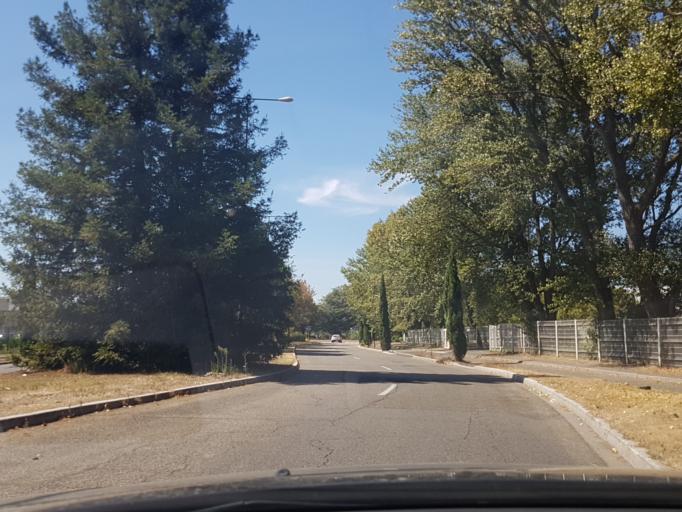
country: FR
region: Provence-Alpes-Cote d'Azur
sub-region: Departement des Bouches-du-Rhone
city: Rognonas
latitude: 43.9210
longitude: 4.8048
